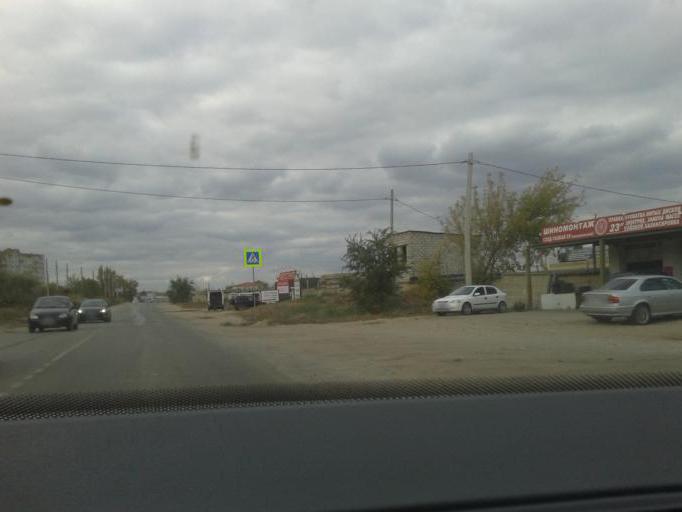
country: RU
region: Volgograd
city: Gorodishche
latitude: 48.7696
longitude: 44.5073
